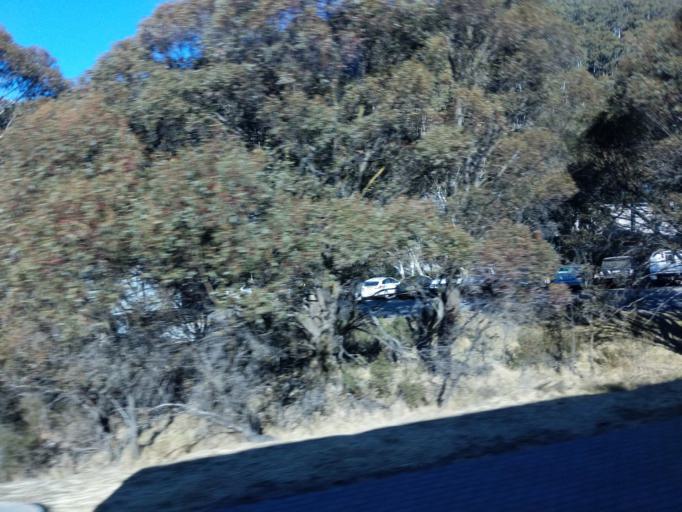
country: AU
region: New South Wales
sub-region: Snowy River
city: Jindabyne
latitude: -36.5007
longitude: 148.3104
